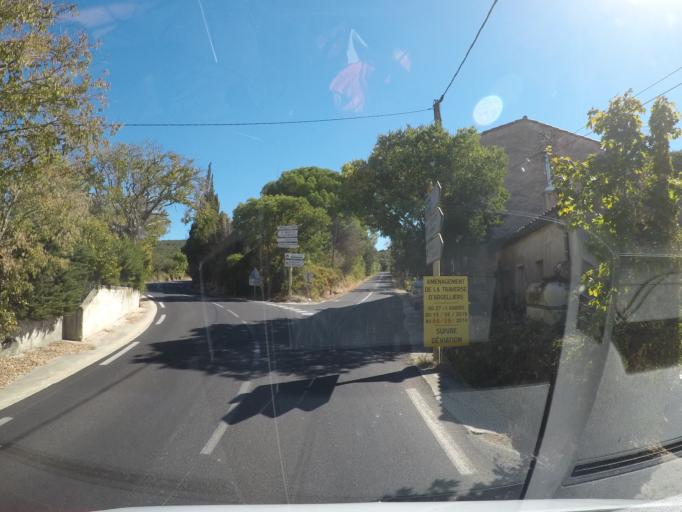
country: FR
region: Languedoc-Roussillon
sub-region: Departement de l'Herault
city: Aniane
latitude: 43.7140
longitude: 3.6208
